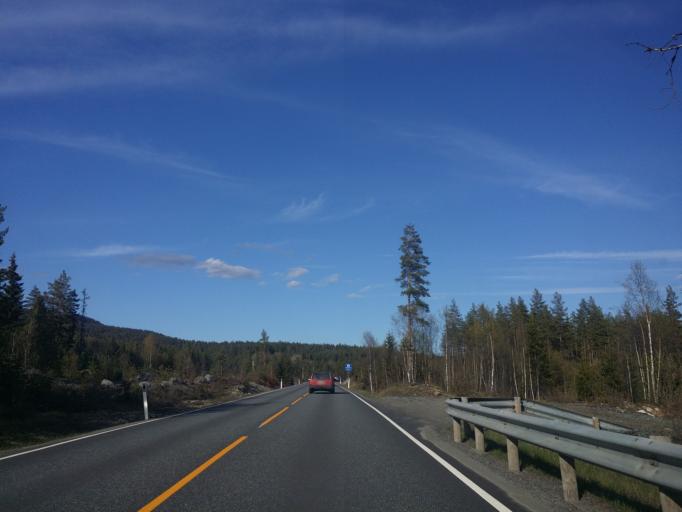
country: NO
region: Buskerud
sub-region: Kongsberg
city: Kongsberg
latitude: 59.6318
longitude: 9.5152
